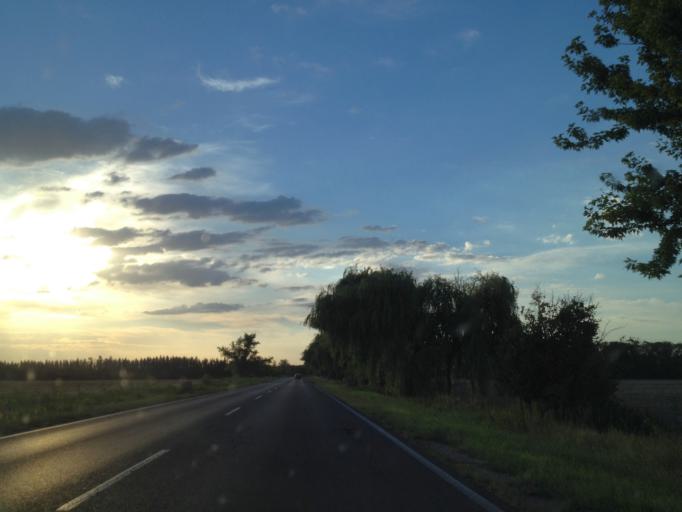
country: HU
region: Gyor-Moson-Sopron
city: Otteveny
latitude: 47.7148
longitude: 17.5123
